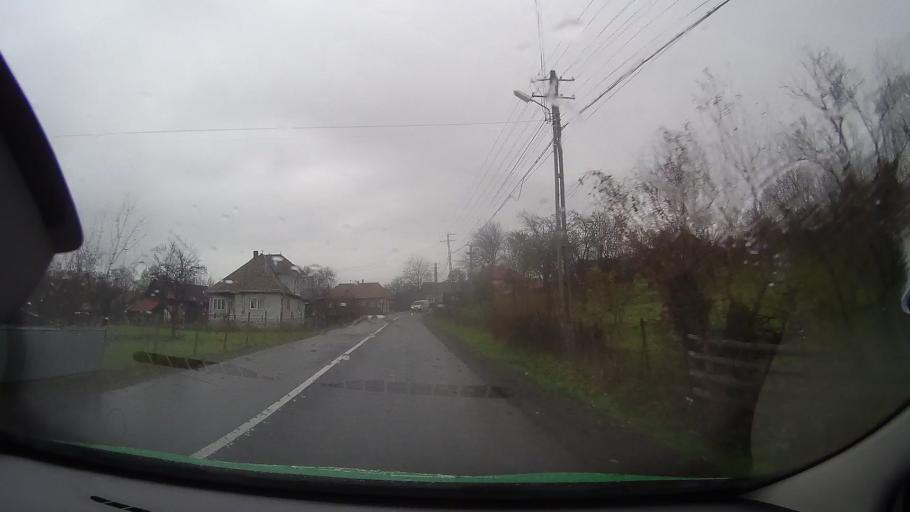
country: RO
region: Mures
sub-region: Comuna Vatava
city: Vatava
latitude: 46.9575
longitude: 24.7627
